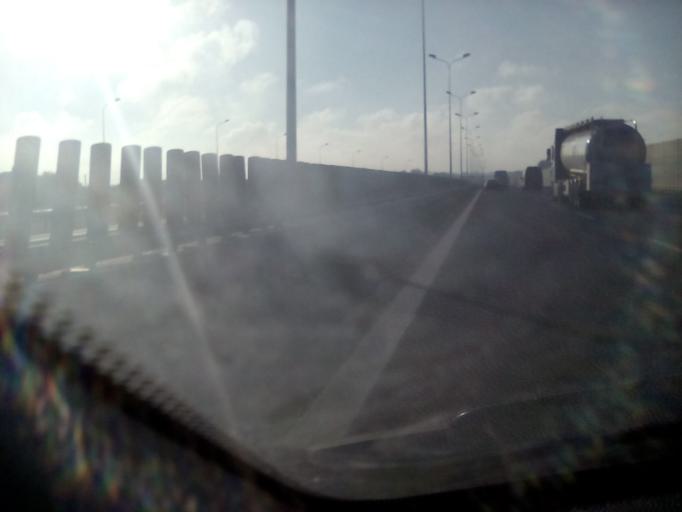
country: PL
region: Masovian Voivodeship
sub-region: Powiat grojecki
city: Grojec
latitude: 51.8256
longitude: 20.8804
